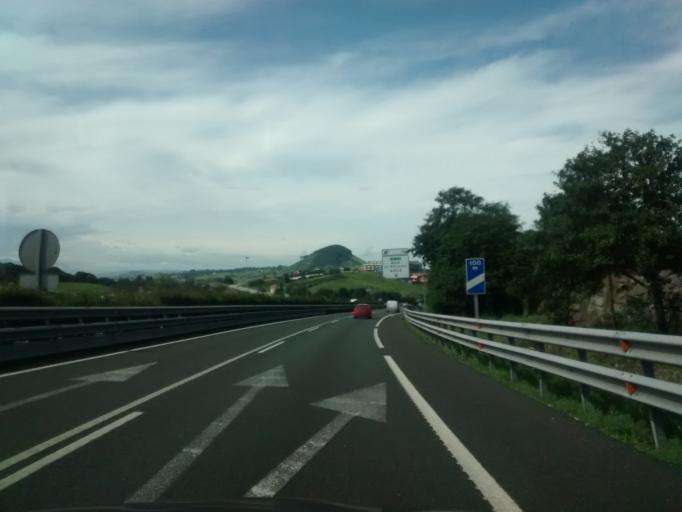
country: ES
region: Cantabria
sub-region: Provincia de Cantabria
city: Santa Cruz de Bezana
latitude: 43.4247
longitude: -3.9386
